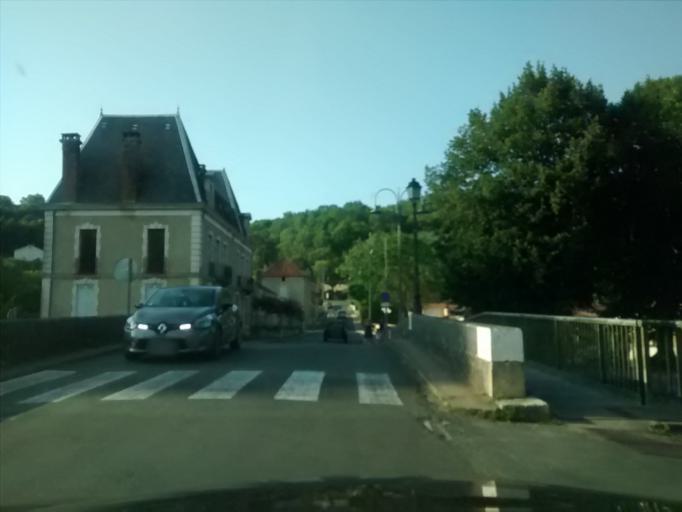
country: FR
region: Aquitaine
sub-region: Departement de la Dordogne
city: Lalinde
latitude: 44.8381
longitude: 0.7382
